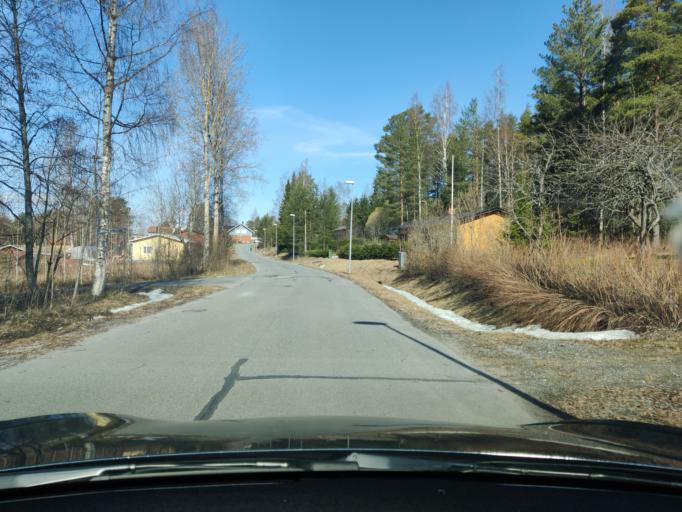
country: FI
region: Northern Savo
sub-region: Kuopio
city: Vehmersalmi
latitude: 62.7591
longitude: 28.0307
